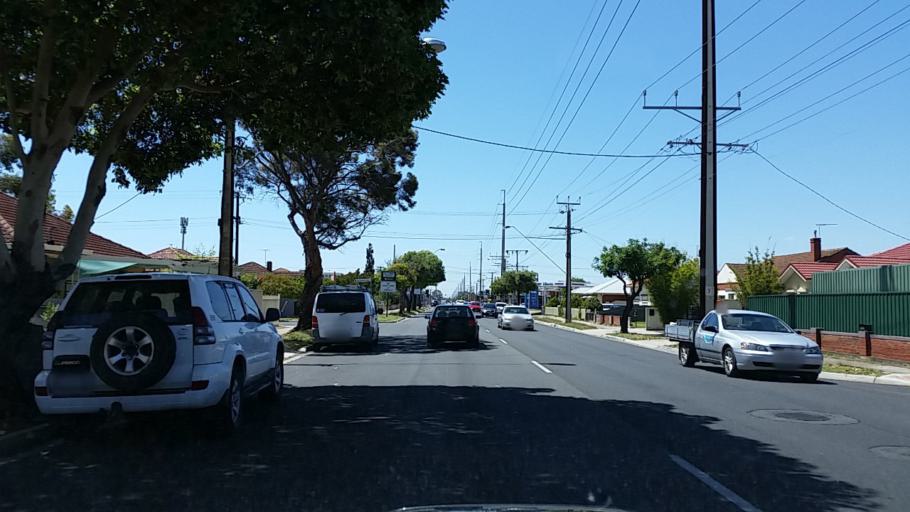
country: AU
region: South Australia
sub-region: Charles Sturt
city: Findon
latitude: -34.8969
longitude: 138.5320
